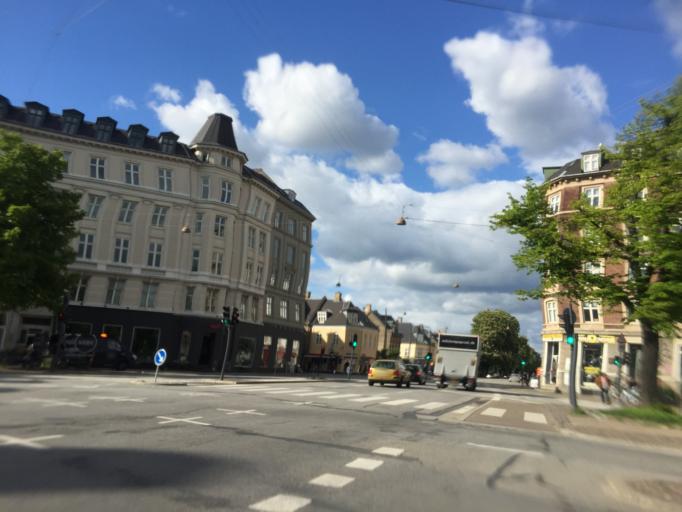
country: DK
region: Capital Region
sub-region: Kobenhavn
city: Copenhagen
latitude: 55.6893
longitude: 12.5745
